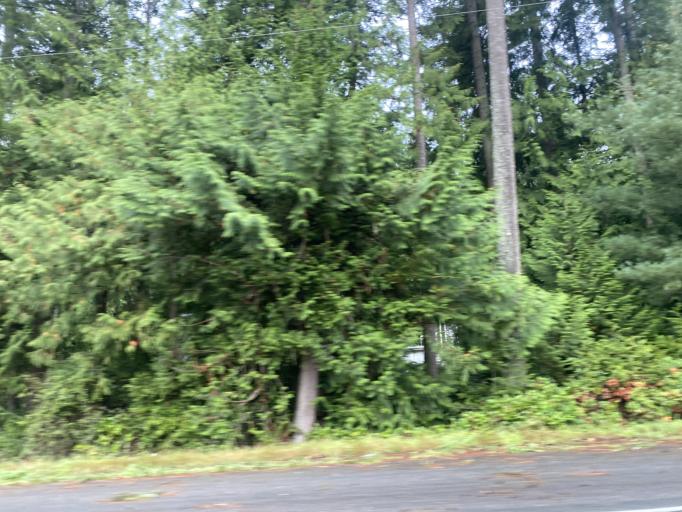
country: US
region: Washington
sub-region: Island County
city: Langley
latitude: 48.0061
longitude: -122.4119
